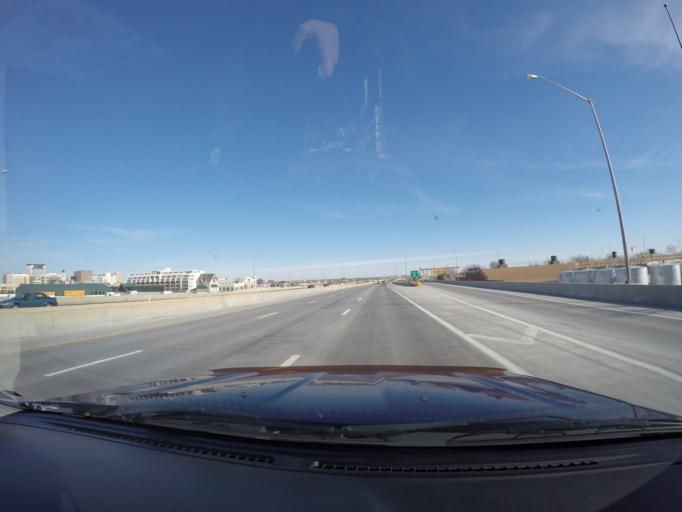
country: US
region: Kansas
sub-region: Sedgwick County
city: Wichita
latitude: 37.6787
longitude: -97.3417
